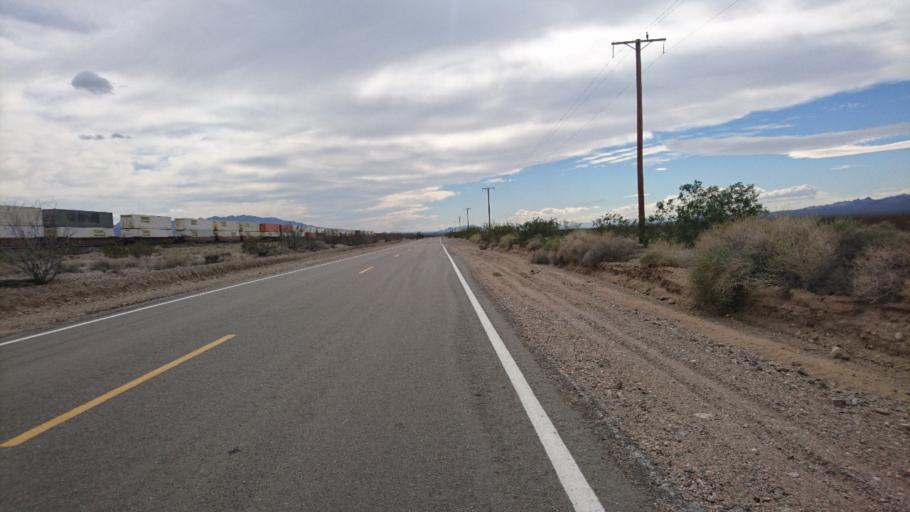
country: US
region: California
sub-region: San Bernardino County
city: Needles
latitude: 34.7864
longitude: -115.2038
